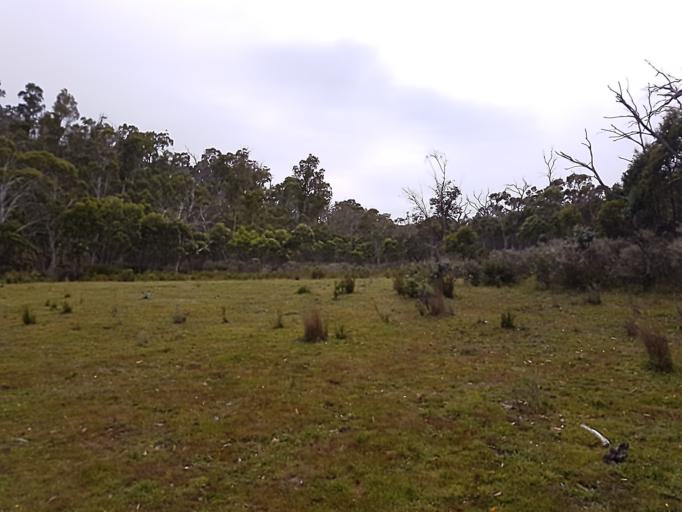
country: AU
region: New South Wales
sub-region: Snowy River
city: Jindabyne
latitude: -36.8049
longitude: 148.1837
